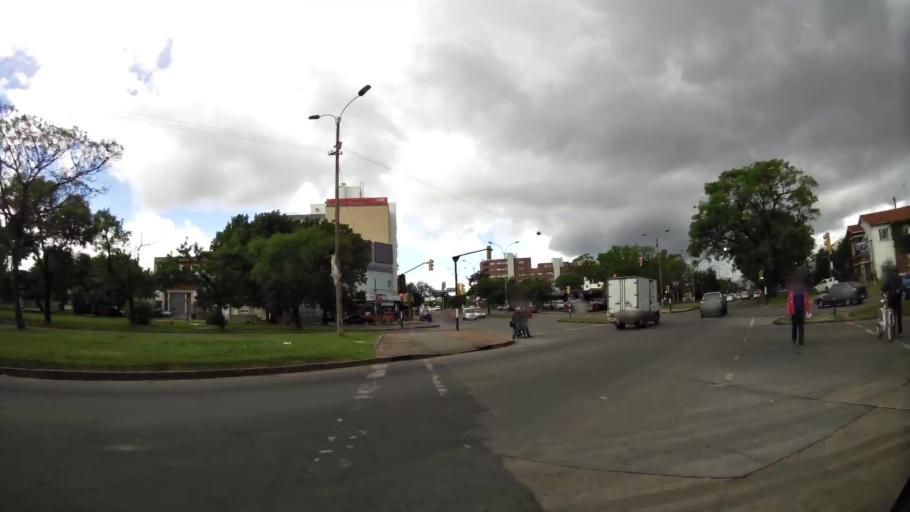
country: UY
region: Montevideo
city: Montevideo
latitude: -34.8756
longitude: -56.1525
